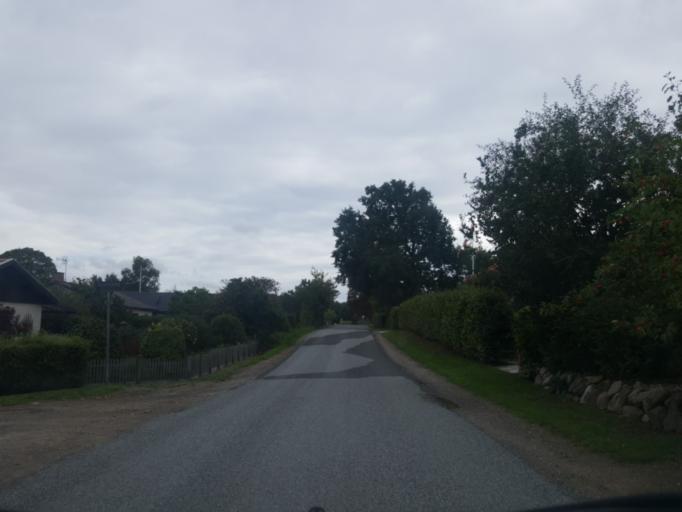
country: DK
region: Zealand
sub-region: Soro Kommune
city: Soro
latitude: 55.4521
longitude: 11.5210
